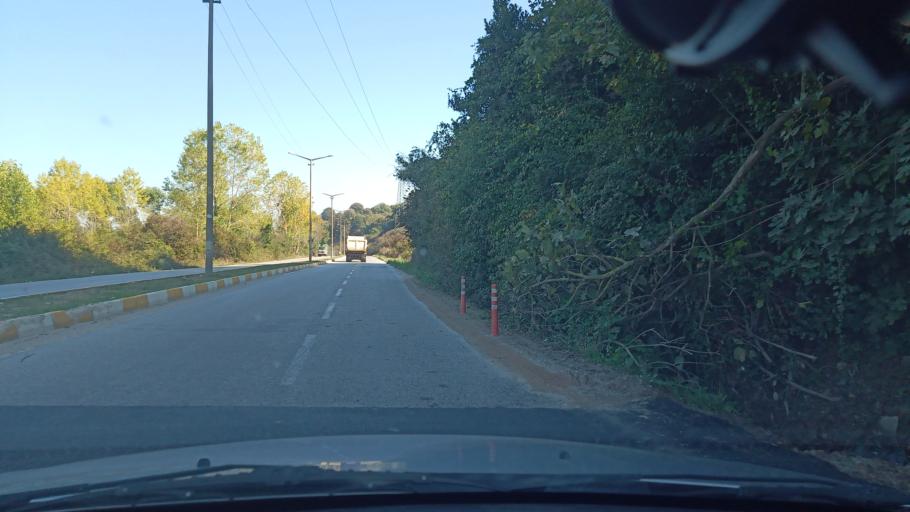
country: TR
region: Sakarya
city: Karasu
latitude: 41.1012
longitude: 30.6611
